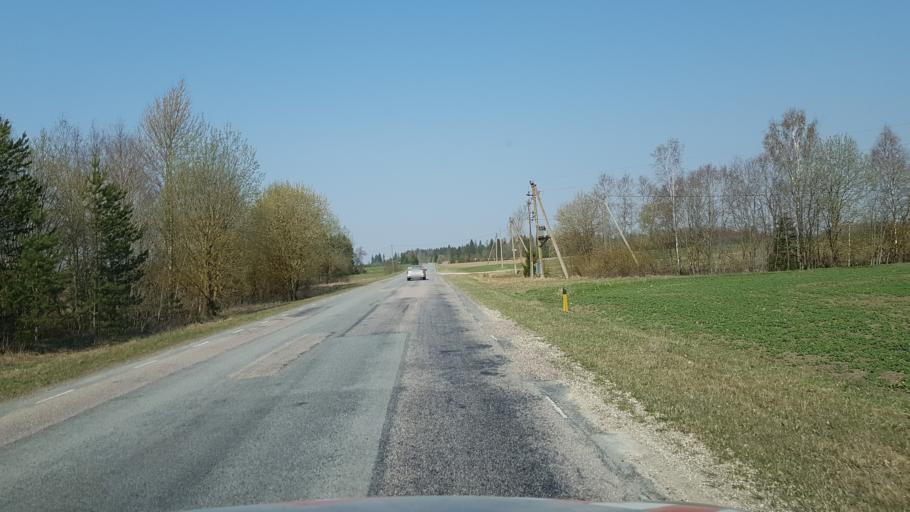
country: EE
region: Raplamaa
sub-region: Rapla vald
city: Rapla
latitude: 59.0244
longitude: 24.7326
